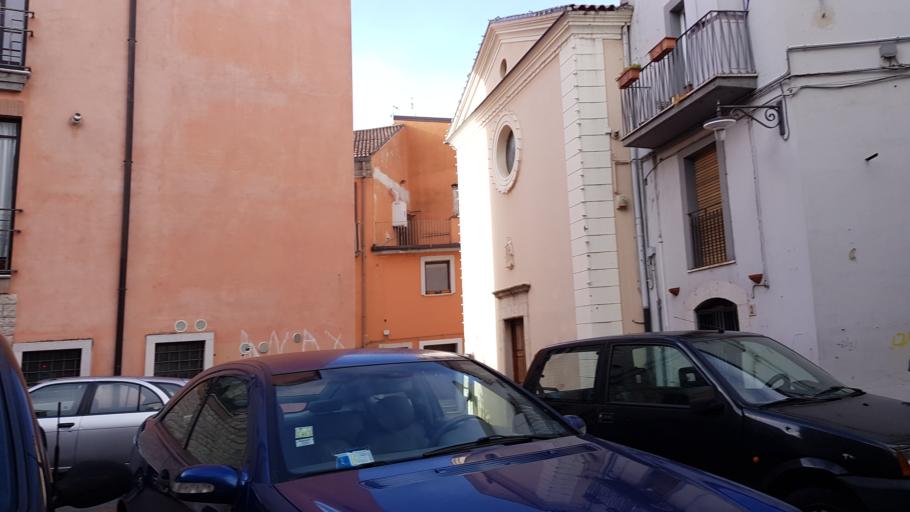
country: IT
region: Basilicate
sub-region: Provincia di Potenza
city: Potenza
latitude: 40.6370
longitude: 15.7995
